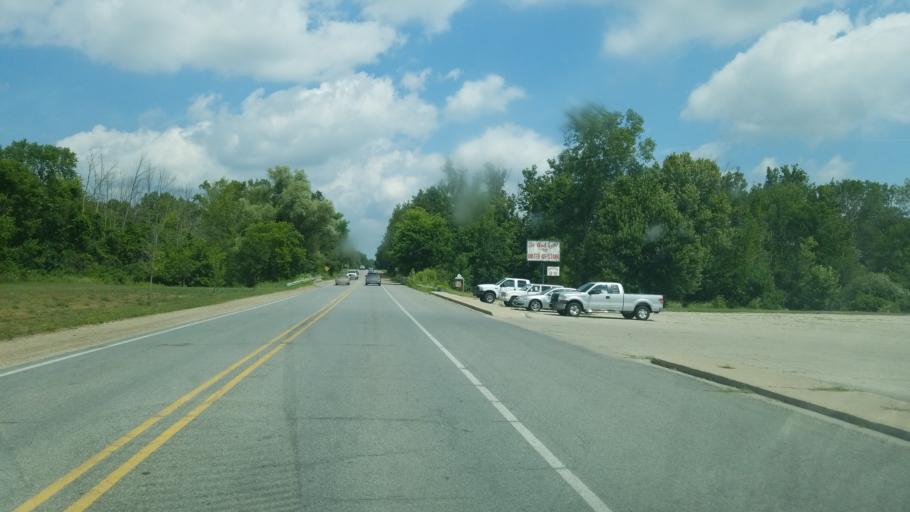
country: US
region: Michigan
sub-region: Montcalm County
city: Howard City
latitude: 43.3997
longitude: -85.4689
